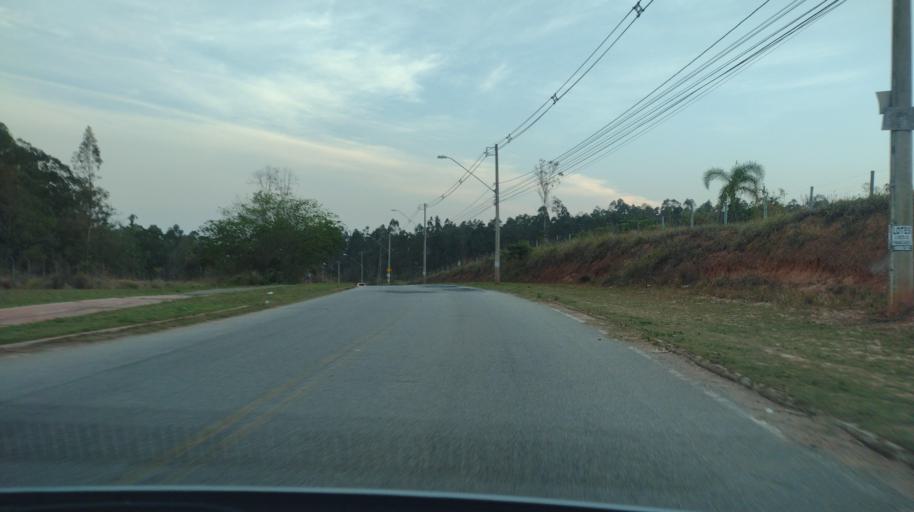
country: BR
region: Sao Paulo
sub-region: Sorocaba
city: Sorocaba
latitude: -23.3750
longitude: -47.4745
